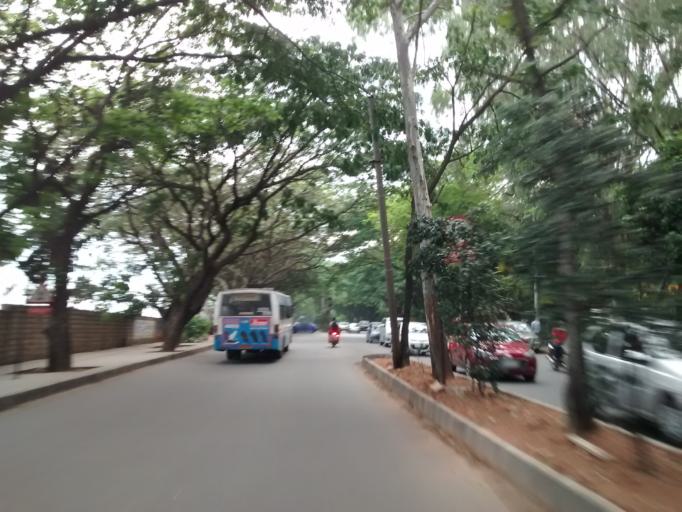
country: IN
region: Karnataka
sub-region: Bangalore Urban
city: Bangalore
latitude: 12.9546
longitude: 77.6831
